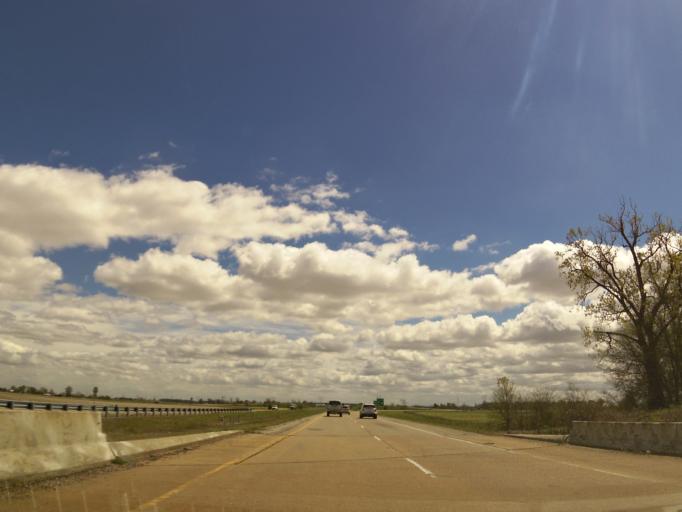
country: US
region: Arkansas
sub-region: Craighead County
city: Bay
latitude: 35.7792
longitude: -90.5925
